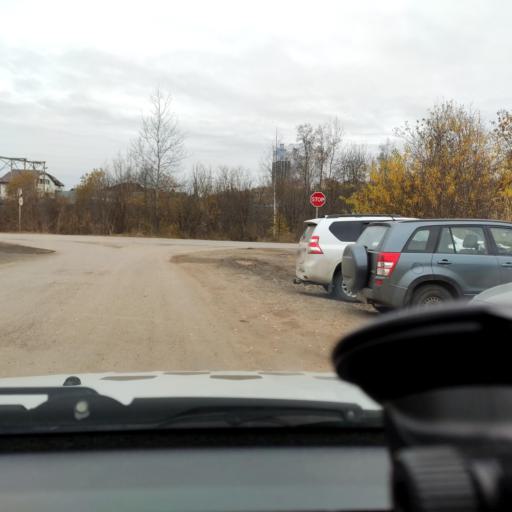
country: RU
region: Perm
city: Perm
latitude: 57.9976
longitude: 56.3202
